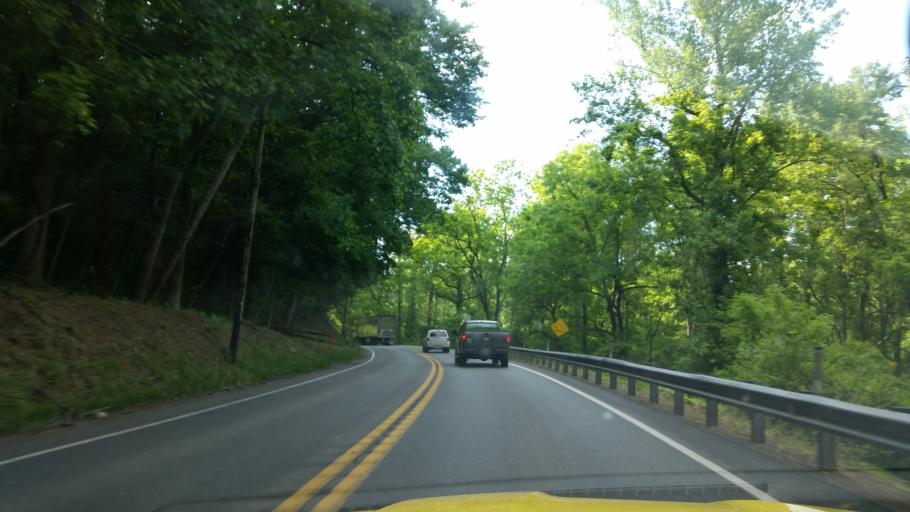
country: US
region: Pennsylvania
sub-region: Lancaster County
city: Brickerville
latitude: 40.2447
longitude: -76.2989
